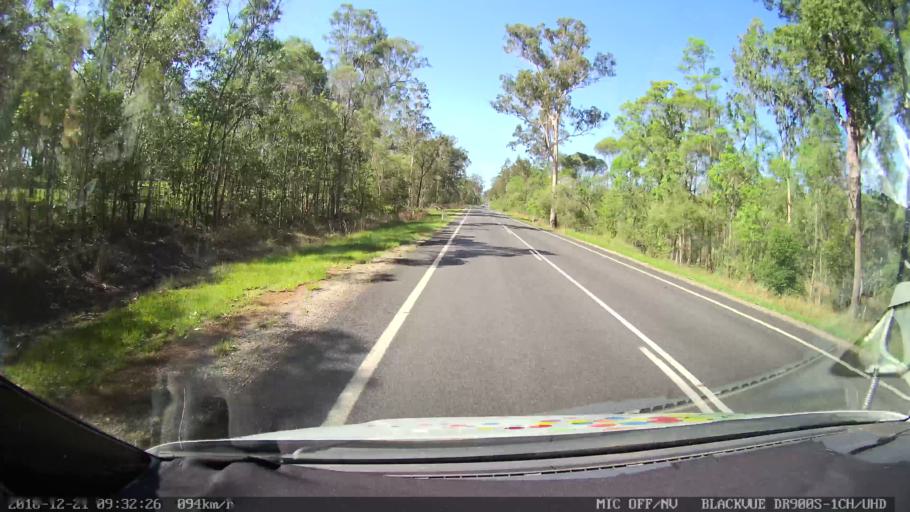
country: AU
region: New South Wales
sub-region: Clarence Valley
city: Maclean
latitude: -29.4705
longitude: 152.9785
